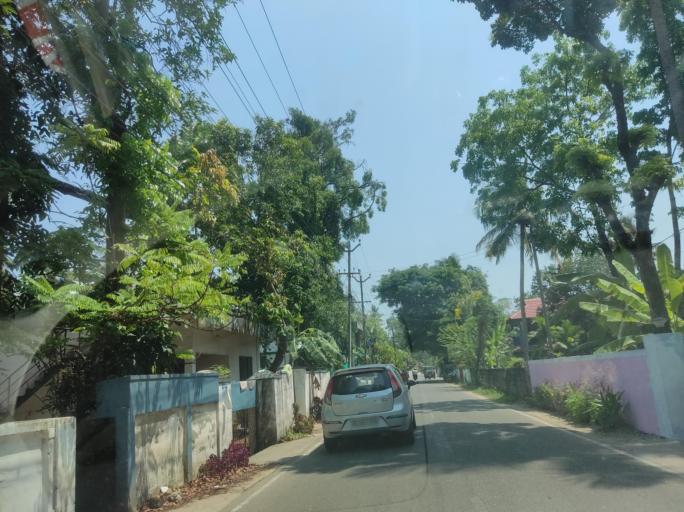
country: IN
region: Kerala
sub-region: Alappuzha
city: Kutiatodu
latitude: 9.8423
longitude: 76.2958
